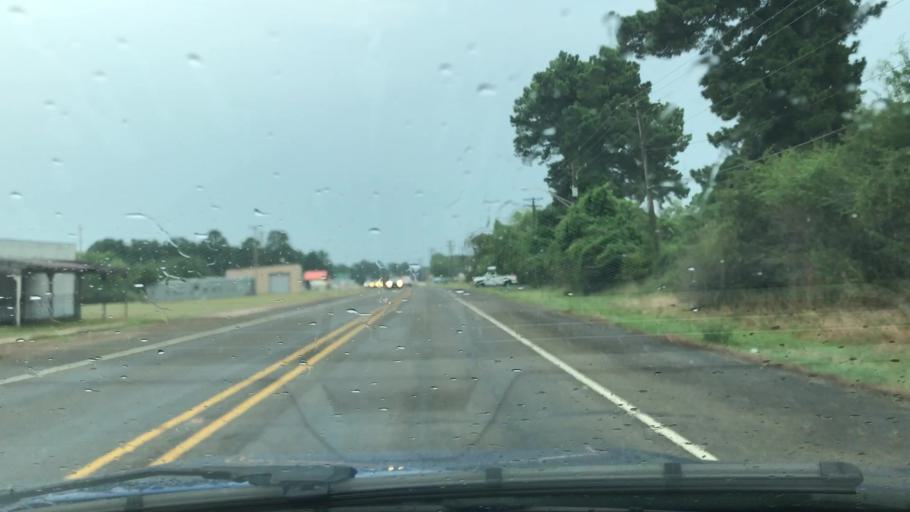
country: US
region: Texas
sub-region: Harrison County
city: Waskom
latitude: 32.4716
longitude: -94.0448
